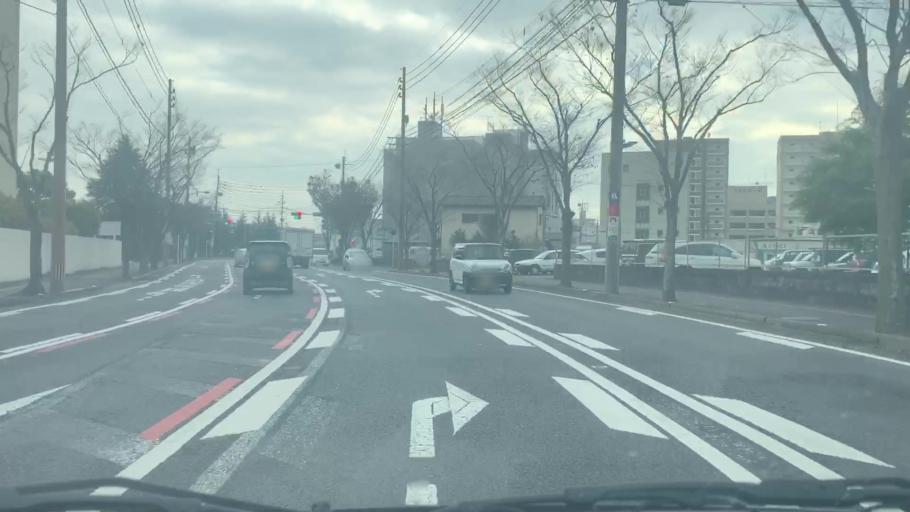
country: JP
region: Saga Prefecture
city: Saga-shi
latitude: 33.2639
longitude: 130.3023
